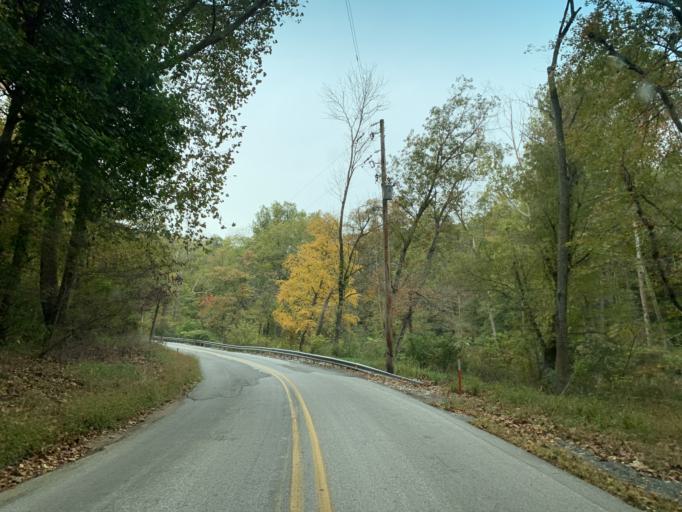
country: US
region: Pennsylvania
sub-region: York County
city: Susquehanna Trails
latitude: 39.7898
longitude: -76.4140
